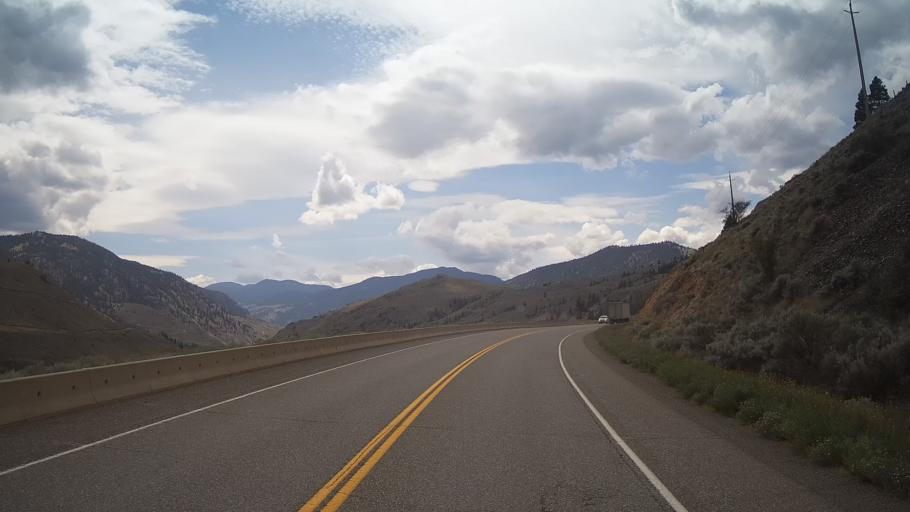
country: CA
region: British Columbia
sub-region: Thompson-Nicola Regional District
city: Ashcroft
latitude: 50.4920
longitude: -121.2962
